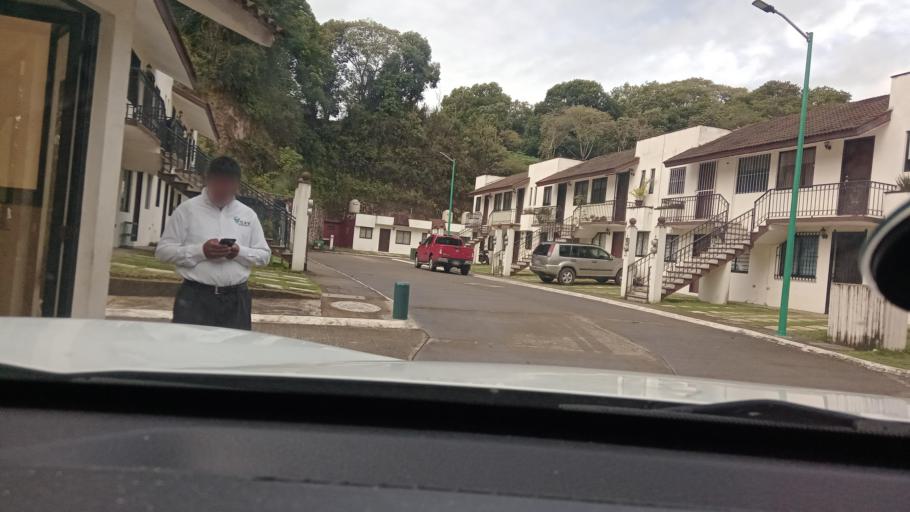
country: MX
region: Veracruz
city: Coatepec
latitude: 19.4402
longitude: -96.9610
